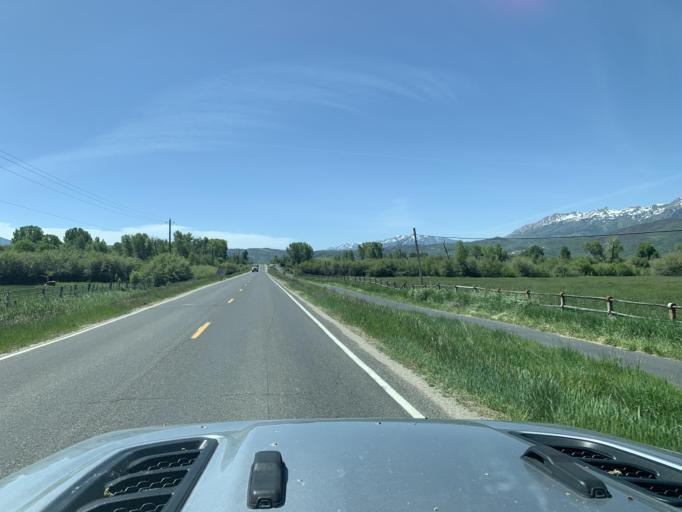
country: US
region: Utah
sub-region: Weber County
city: Wolf Creek
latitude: 41.2896
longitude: -111.7770
